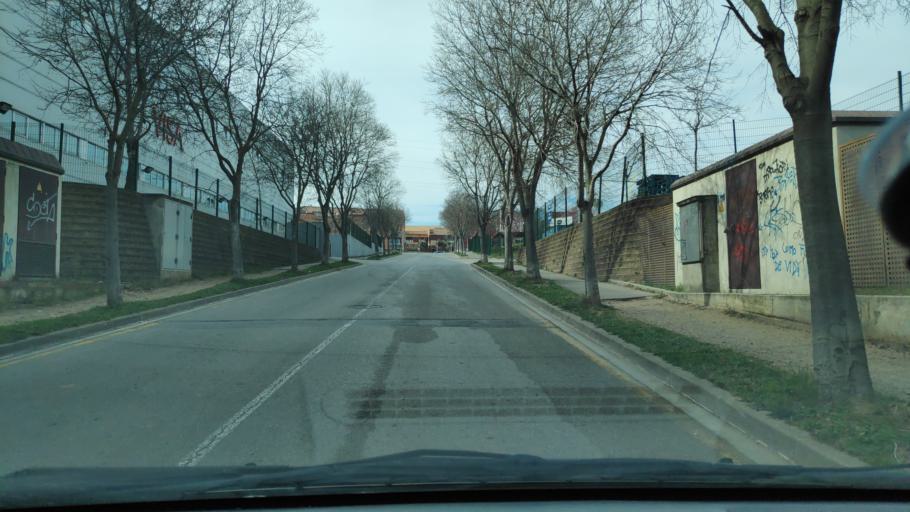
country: ES
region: Catalonia
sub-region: Provincia de Barcelona
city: Rubi
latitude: 41.4857
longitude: 2.0433
